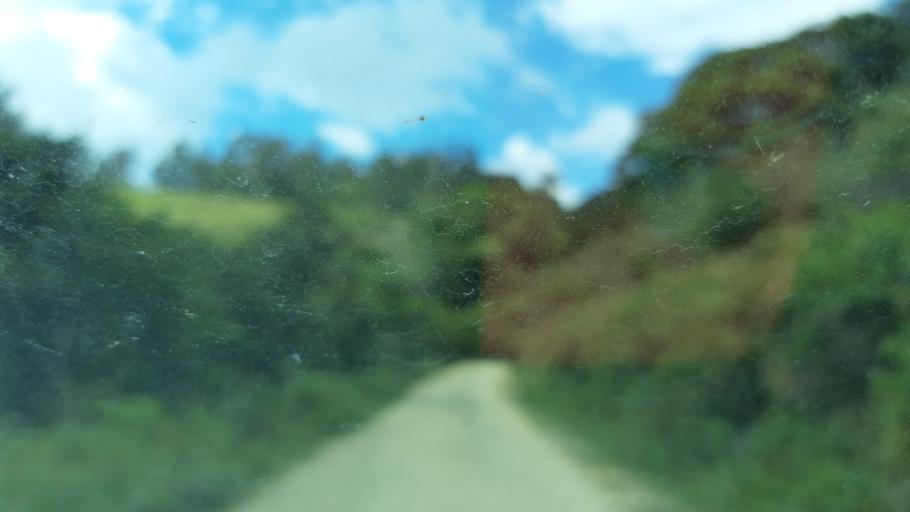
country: CO
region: Boyaca
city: Santa Sofia
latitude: 5.7216
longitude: -73.5410
